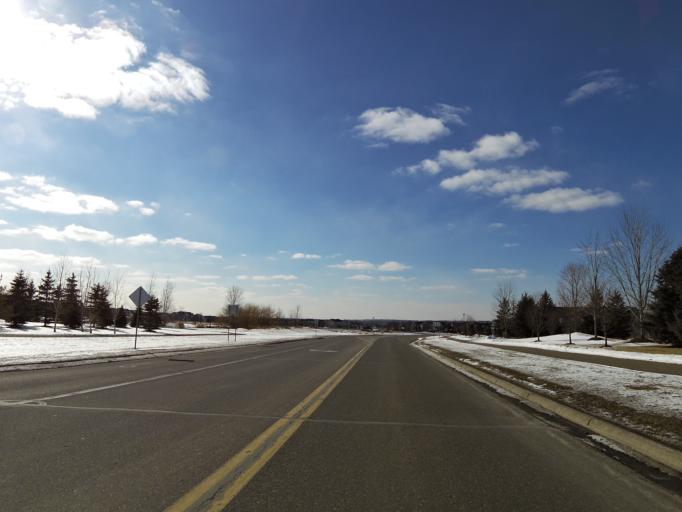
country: US
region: Minnesota
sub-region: Washington County
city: Afton
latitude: 44.9020
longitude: -92.8713
